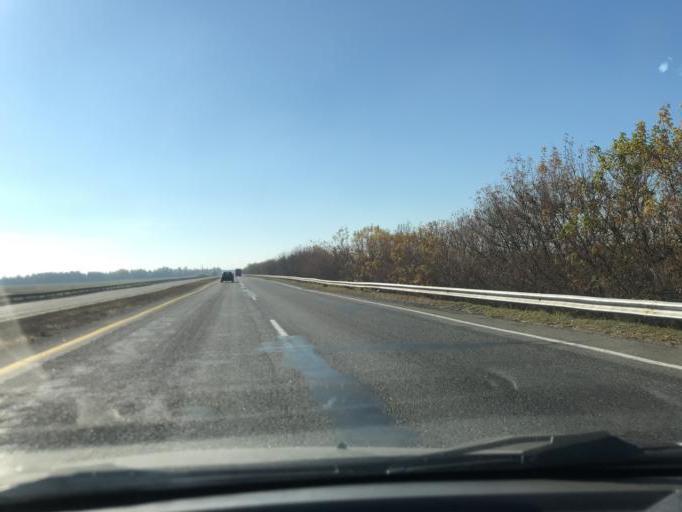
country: BY
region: Gomel
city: Horad Rechytsa
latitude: 52.3089
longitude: 30.5016
